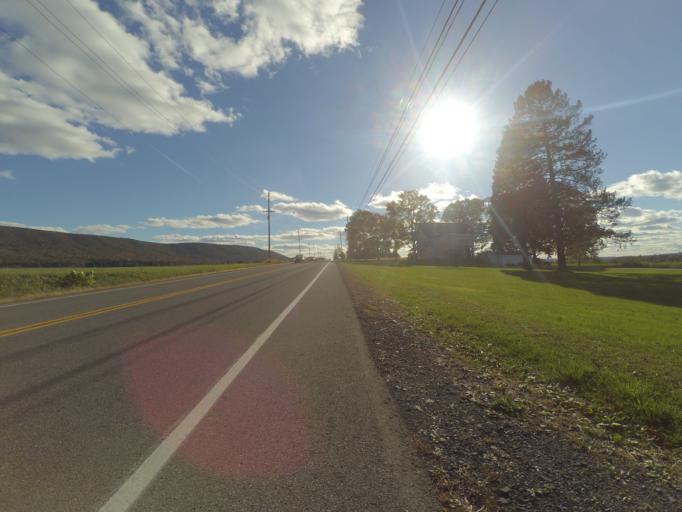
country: US
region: Pennsylvania
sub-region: Centre County
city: Pleasant Gap
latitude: 40.8528
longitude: -77.7898
